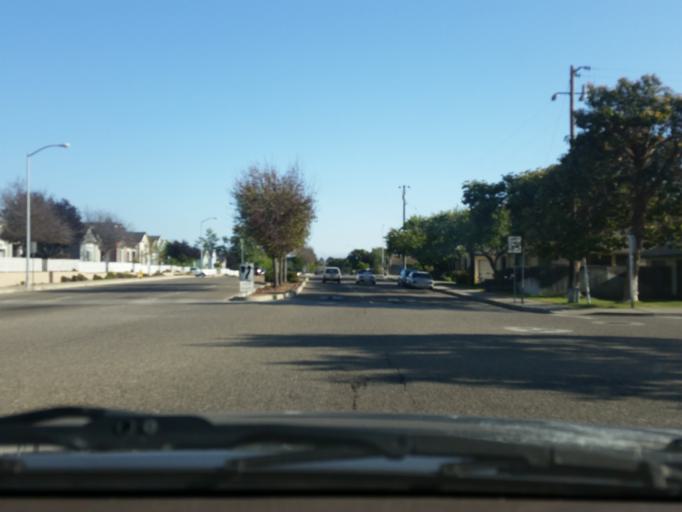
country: US
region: California
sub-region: San Luis Obispo County
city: Grover Beach
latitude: 35.1181
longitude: -120.6094
